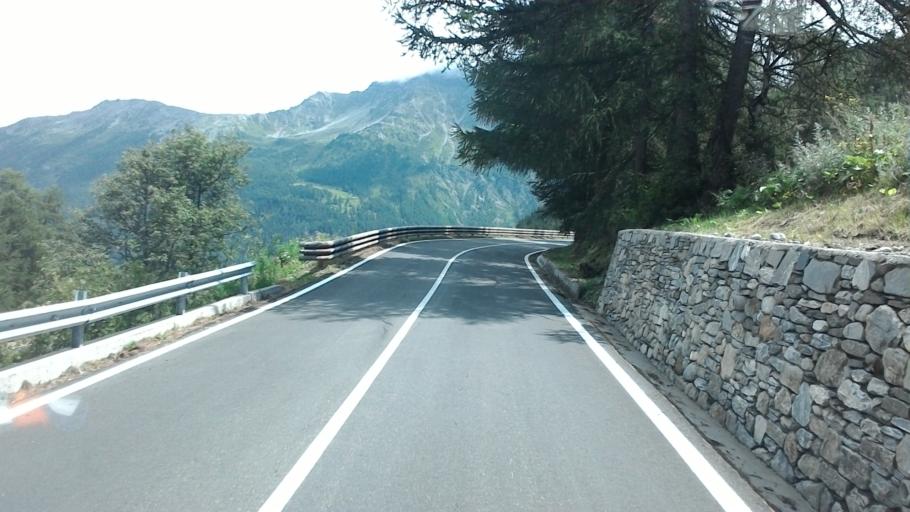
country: IT
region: Aosta Valley
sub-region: Valle d'Aosta
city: La Thuile
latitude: 45.7088
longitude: 6.9294
